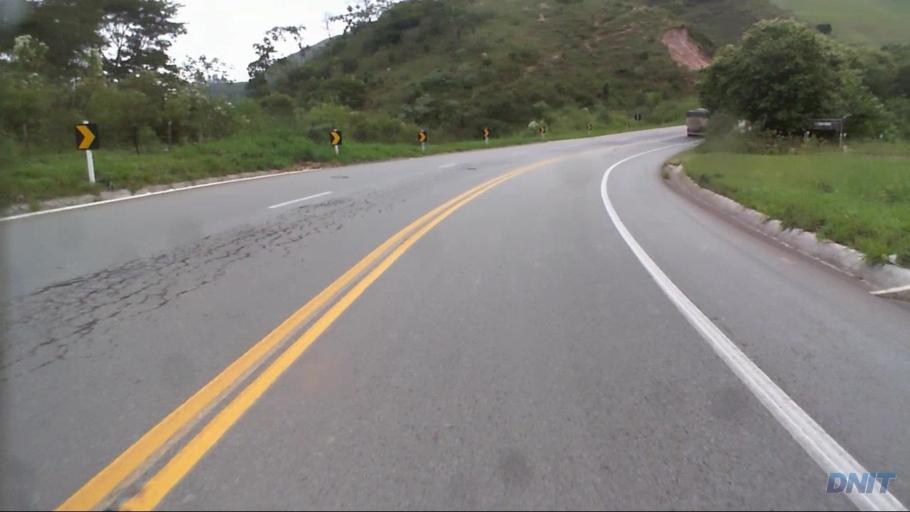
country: BR
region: Minas Gerais
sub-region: Nova Era
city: Nova Era
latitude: -19.6750
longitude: -42.9749
